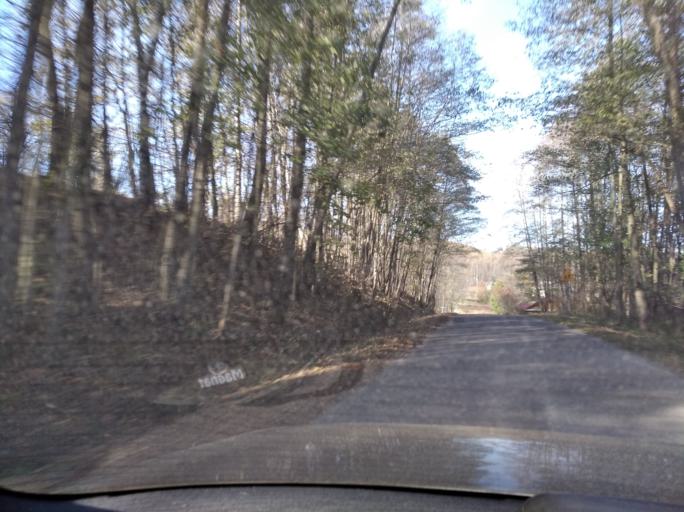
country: PL
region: Subcarpathian Voivodeship
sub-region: Powiat ropczycko-sedziszowski
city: Wielopole Skrzynskie
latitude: 49.9069
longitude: 21.5678
